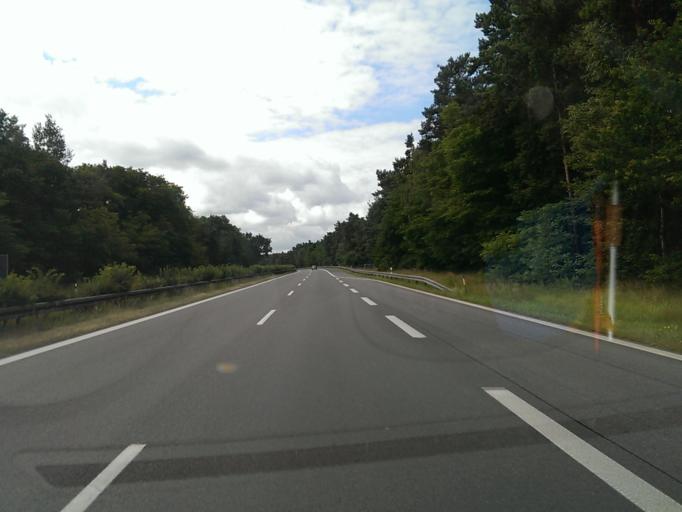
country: DE
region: Brandenburg
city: Lubbenau
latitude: 51.8133
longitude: 13.8915
